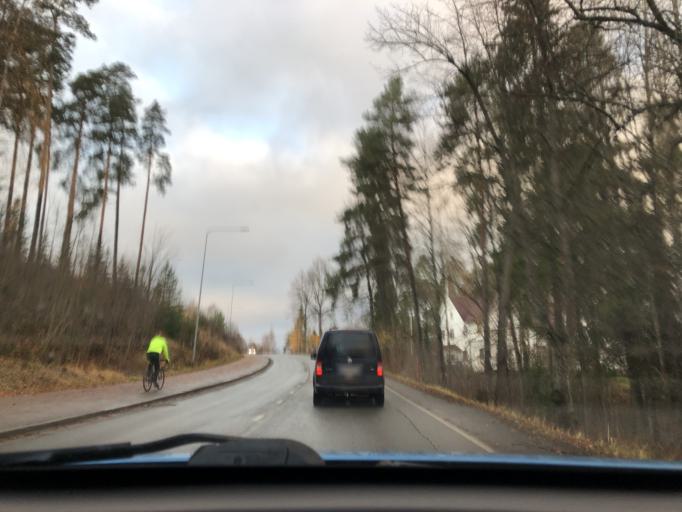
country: FI
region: Pirkanmaa
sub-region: Tampere
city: Kangasala
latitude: 61.4666
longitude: 24.0664
